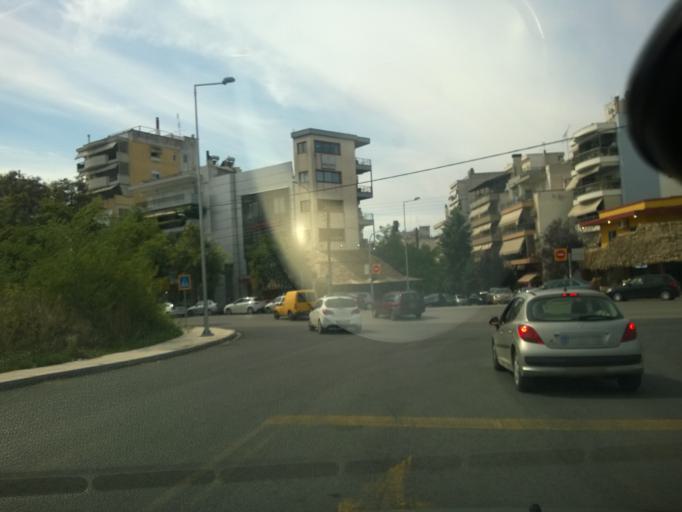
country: GR
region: Central Macedonia
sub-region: Nomos Thessalonikis
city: Kalamaria
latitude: 40.5908
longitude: 22.9545
